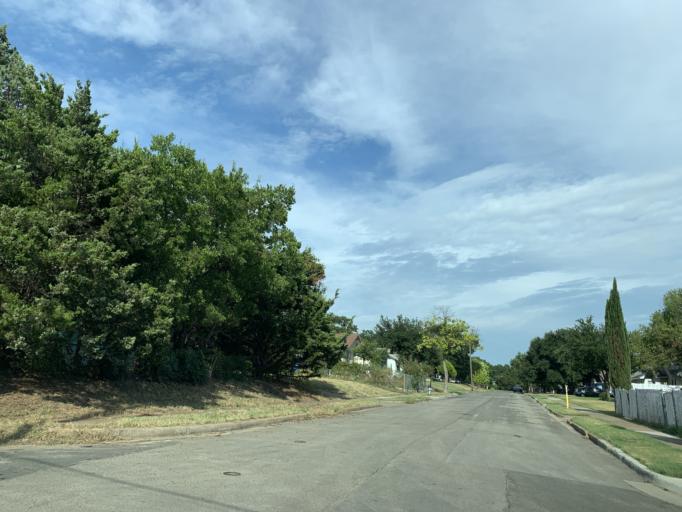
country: US
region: Texas
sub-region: Dallas County
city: Cockrell Hill
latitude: 32.7363
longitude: -96.8343
